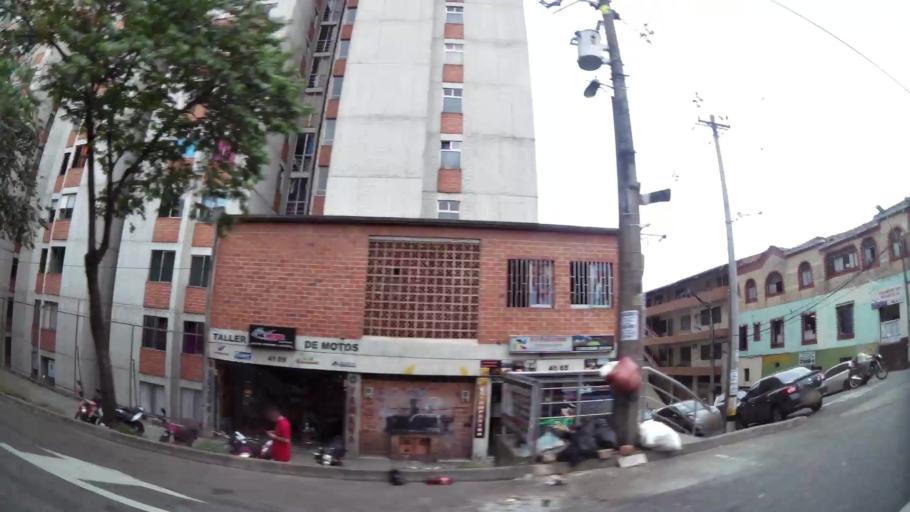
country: CO
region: Antioquia
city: Medellin
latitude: 6.2416
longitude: -75.5685
